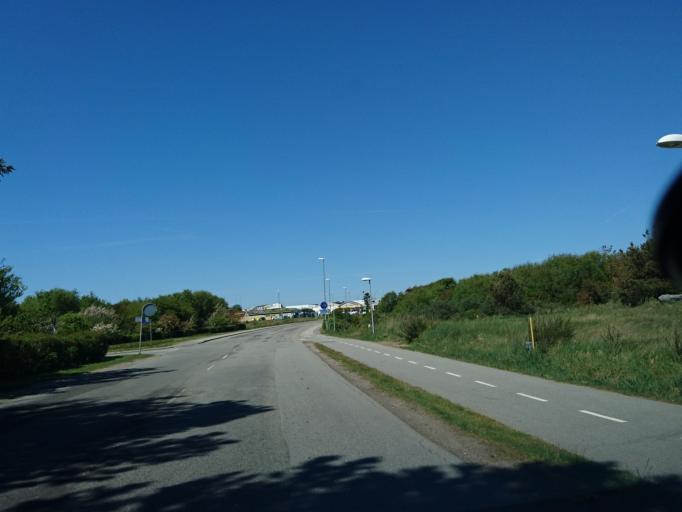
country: DK
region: North Denmark
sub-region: Hjorring Kommune
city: Hirtshals
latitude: 57.5799
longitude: 9.9724
